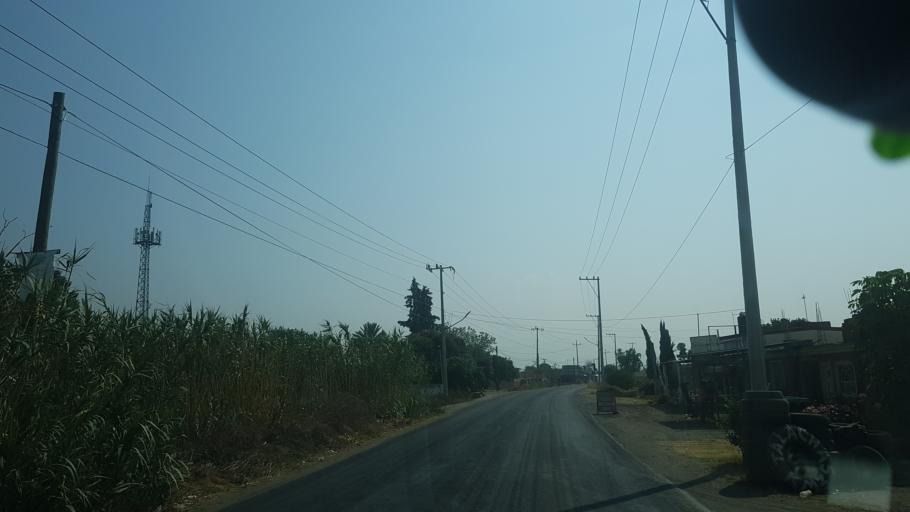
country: MX
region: Puebla
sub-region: San Jeronimo Tecuanipan
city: Los Reyes Tlanechicolpan
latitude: 19.0521
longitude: -98.3457
